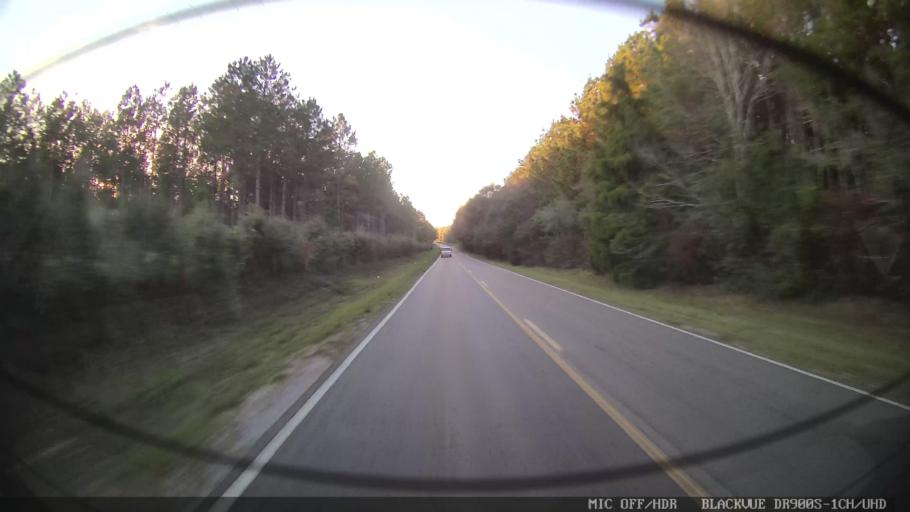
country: US
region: Mississippi
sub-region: Lamar County
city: Lumberton
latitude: 30.9986
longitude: -89.4059
